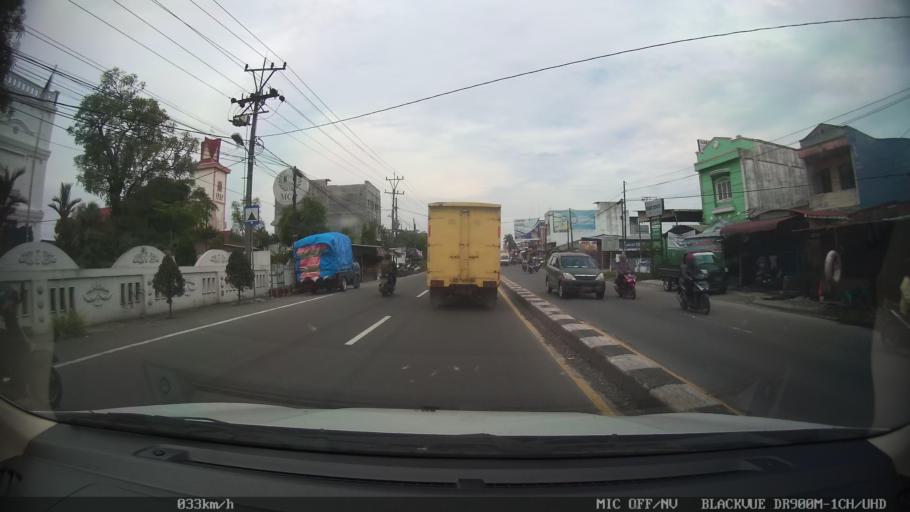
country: ID
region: North Sumatra
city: Sunggal
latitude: 3.5995
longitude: 98.5551
